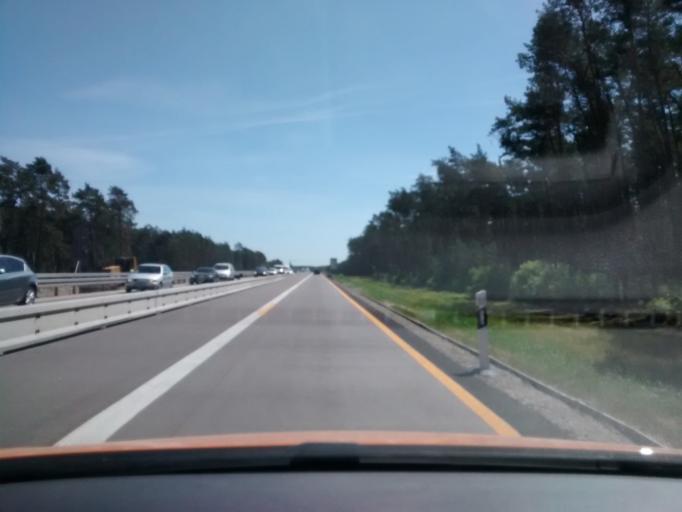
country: DE
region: Brandenburg
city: Spreenhagen
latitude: 52.3143
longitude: 13.8044
